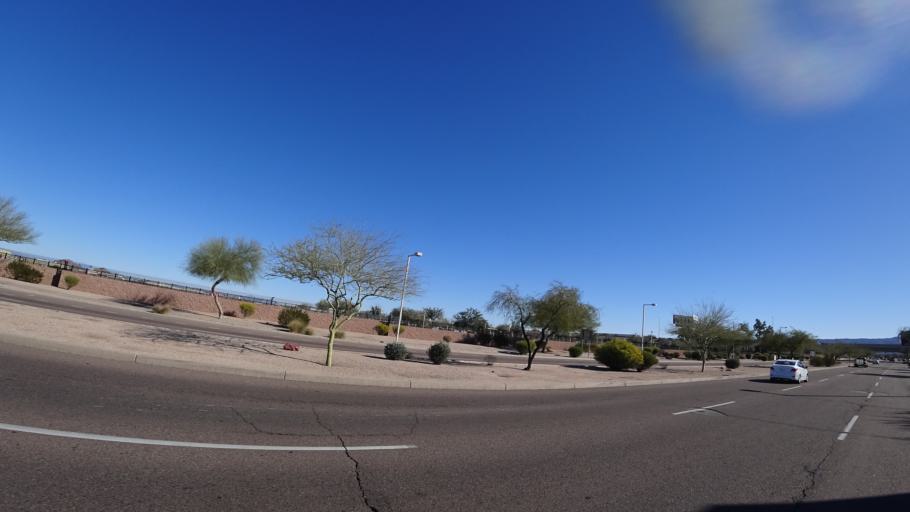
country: US
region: Arizona
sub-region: Maricopa County
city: Phoenix
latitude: 33.4401
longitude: -112.0348
